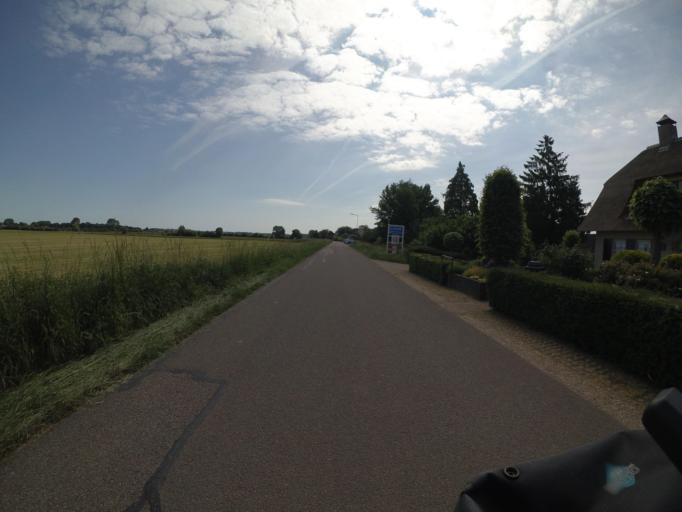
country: NL
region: Gelderland
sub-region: Gemeente Rheden
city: Rheden
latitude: 51.9883
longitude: 6.0169
